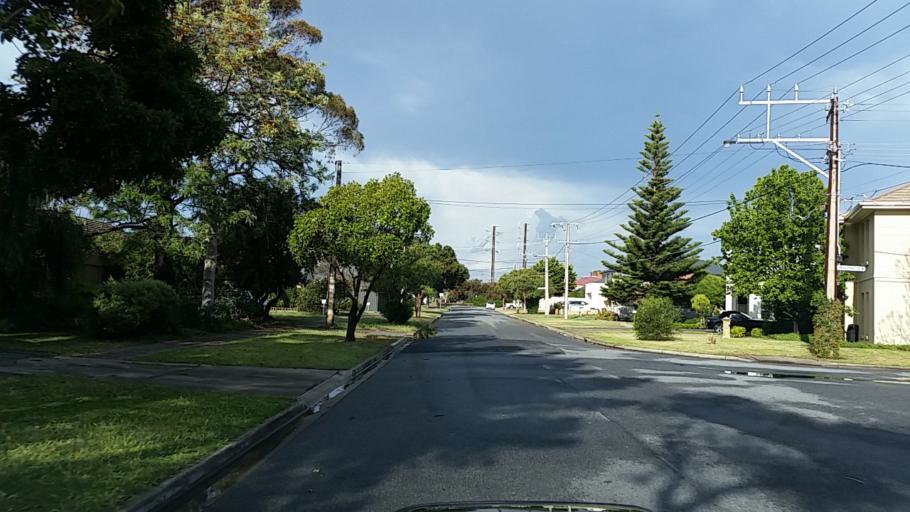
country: AU
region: South Australia
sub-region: Charles Sturt
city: Grange
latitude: -34.9035
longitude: 138.5035
